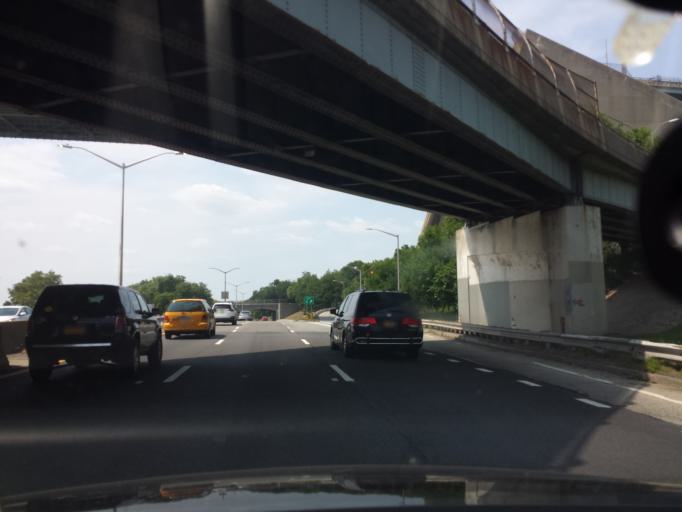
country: US
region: New York
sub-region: Kings County
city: Bensonhurst
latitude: 40.6088
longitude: -74.0344
